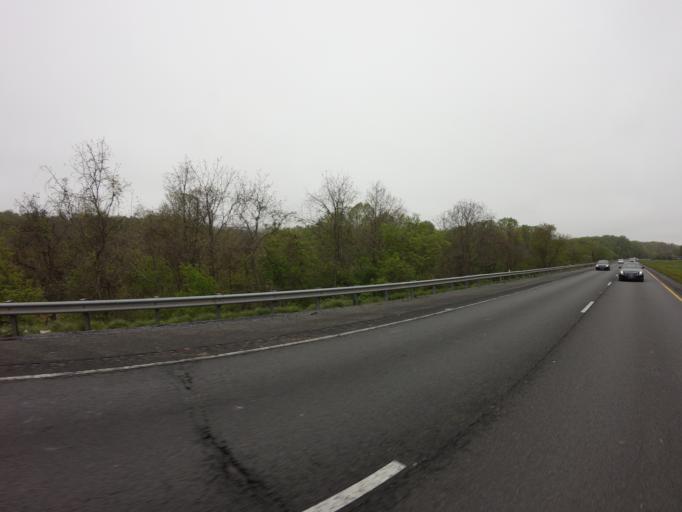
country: US
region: Maryland
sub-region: Frederick County
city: Myersville
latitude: 39.5196
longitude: -77.5992
